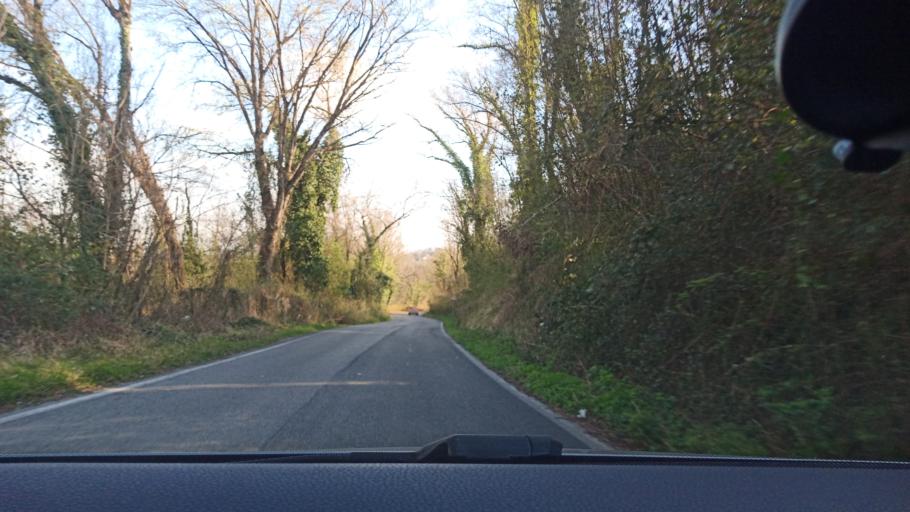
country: IT
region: Latium
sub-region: Citta metropolitana di Roma Capitale
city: Torrita Tiberina
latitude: 42.2453
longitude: 12.6200
